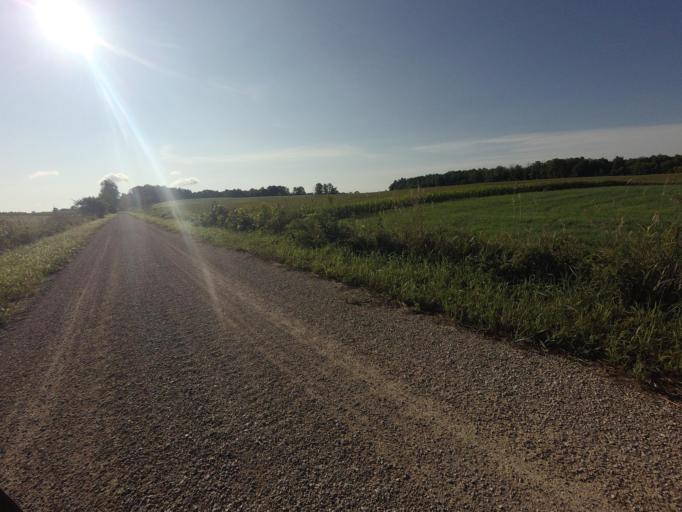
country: CA
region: Ontario
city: Huron East
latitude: 43.7429
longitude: -81.4856
